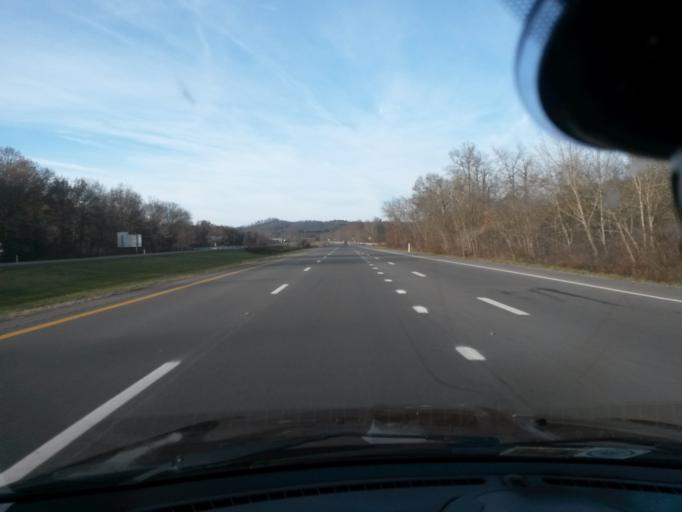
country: US
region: West Virginia
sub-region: Greenbrier County
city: Rainelle
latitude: 37.9029
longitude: -80.6374
